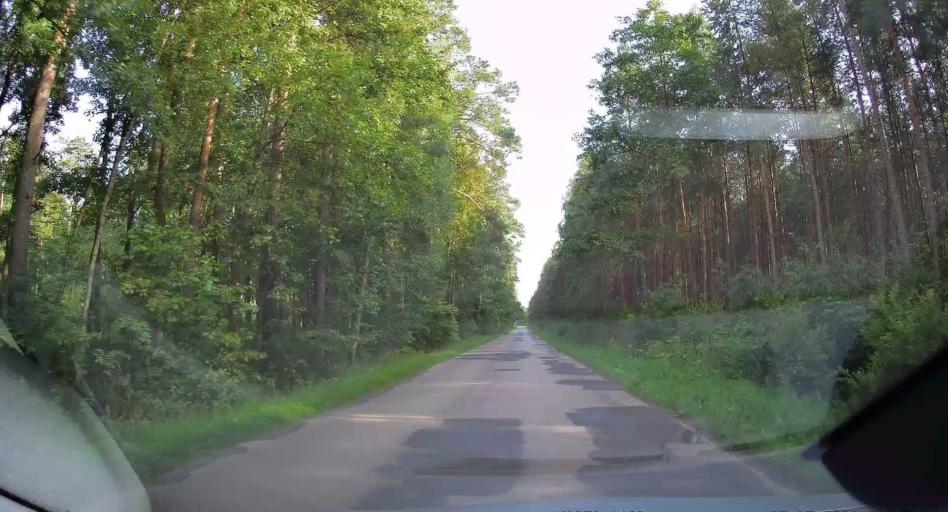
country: PL
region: Swietokrzyskie
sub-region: Powiat konecki
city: Konskie
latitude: 51.2319
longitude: 20.3826
